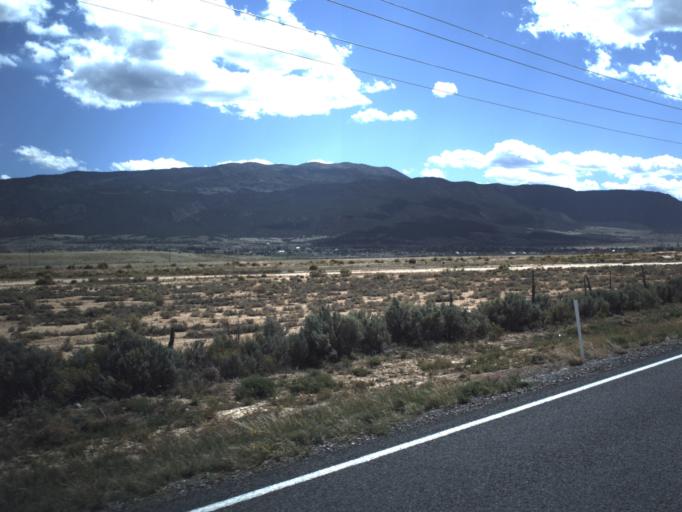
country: US
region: Utah
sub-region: Iron County
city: Enoch
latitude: 37.7927
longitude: -113.0507
